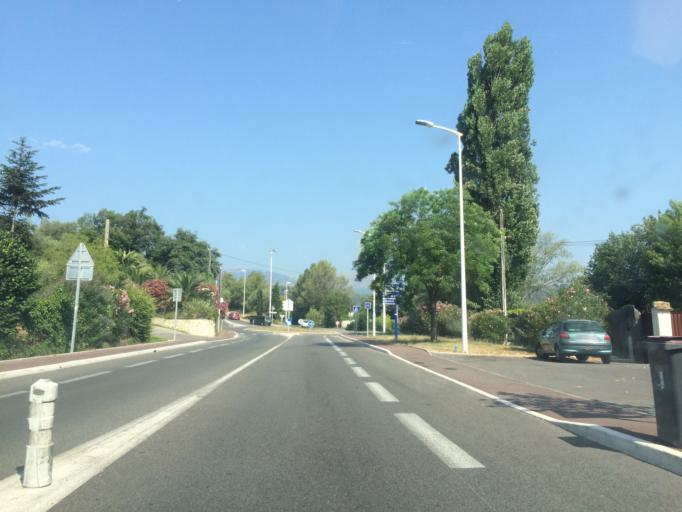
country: FR
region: Provence-Alpes-Cote d'Azur
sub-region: Departement des Alpes-Maritimes
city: La Colle-sur-Loup
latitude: 43.6831
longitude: 7.1161
